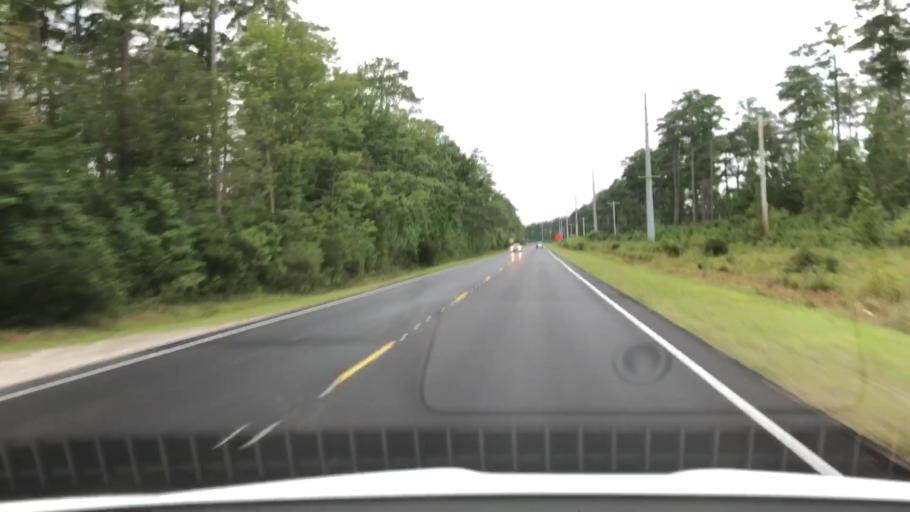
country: US
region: North Carolina
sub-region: Onslow County
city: Swansboro
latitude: 34.7816
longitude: -77.1104
